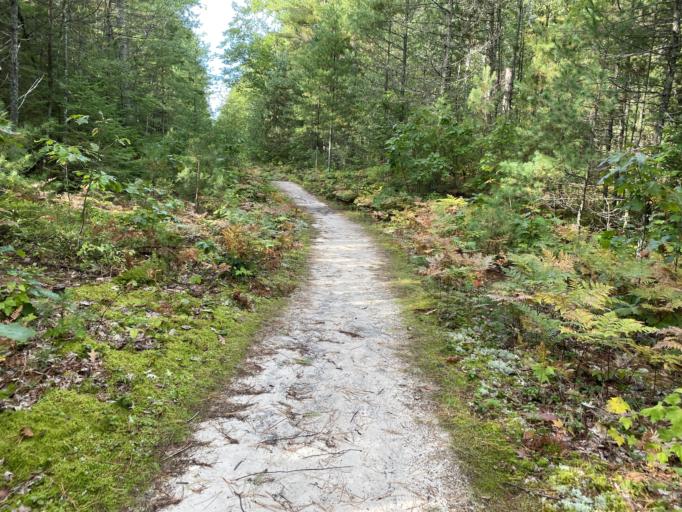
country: US
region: Michigan
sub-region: Mackinac County
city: Saint Ignace
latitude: 45.7489
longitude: -84.8865
